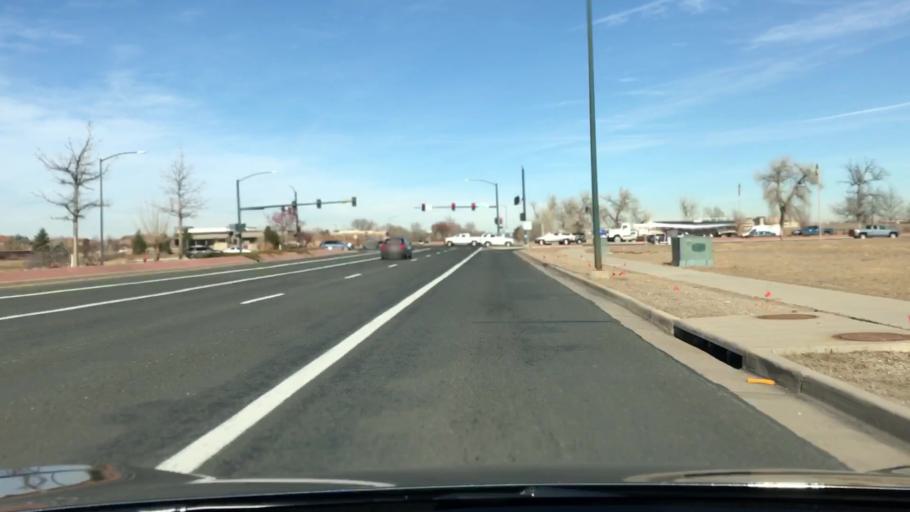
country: US
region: Colorado
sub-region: Adams County
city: Northglenn
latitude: 39.9420
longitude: -104.9966
